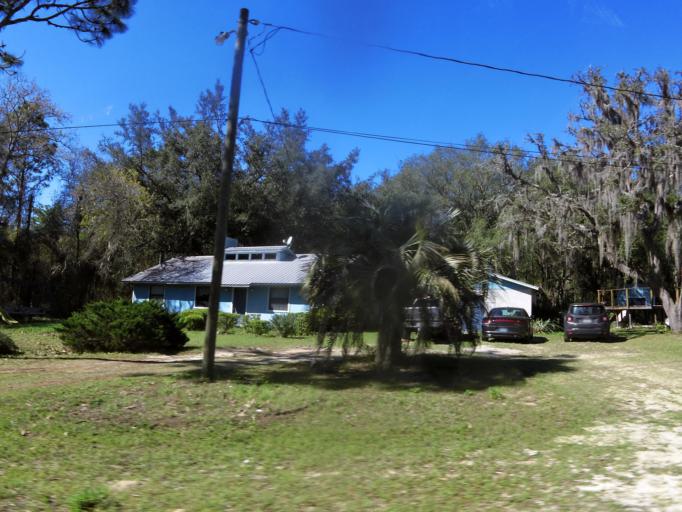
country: US
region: Florida
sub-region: Clay County
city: Keystone Heights
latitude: 29.8020
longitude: -82.0469
